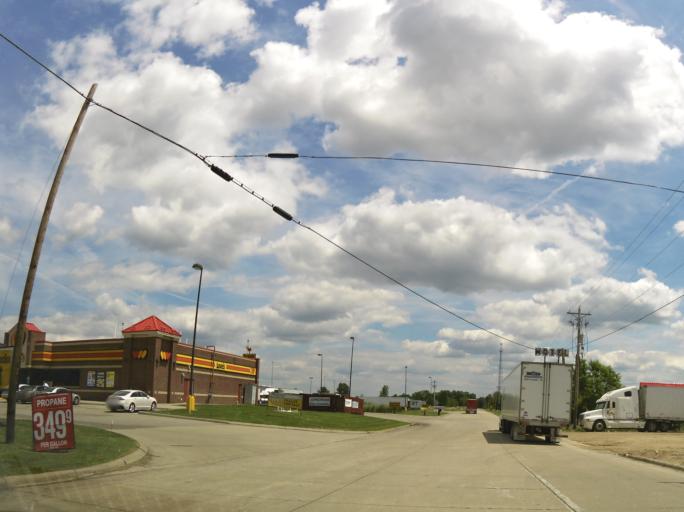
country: US
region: Ohio
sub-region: Medina County
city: Lodi
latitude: 40.9959
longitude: -81.9957
